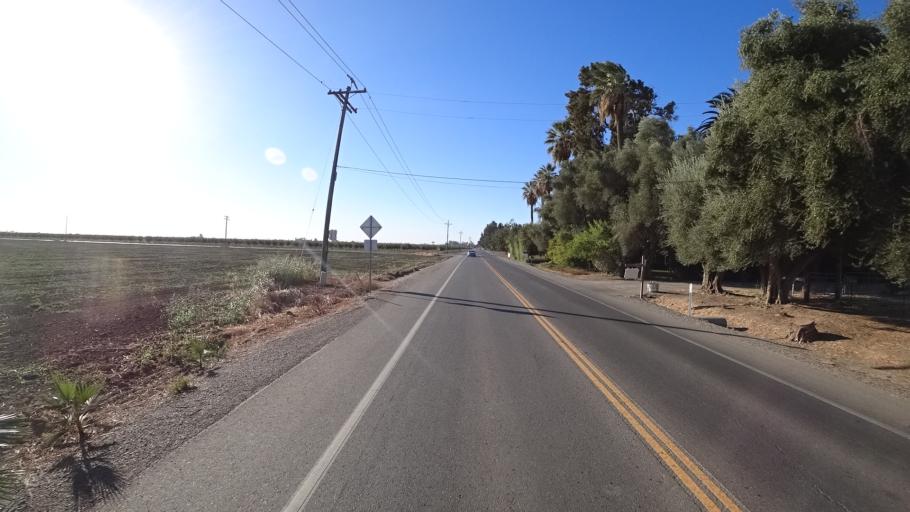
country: US
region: California
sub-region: Yolo County
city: Woodland
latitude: 38.6422
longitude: -121.7846
